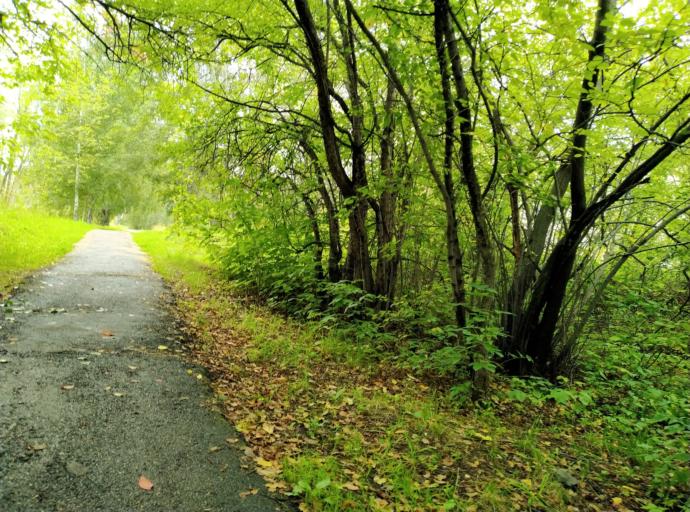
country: RU
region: Krasnoyarskiy
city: Krasnoyarsk
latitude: 55.9881
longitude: 92.7620
